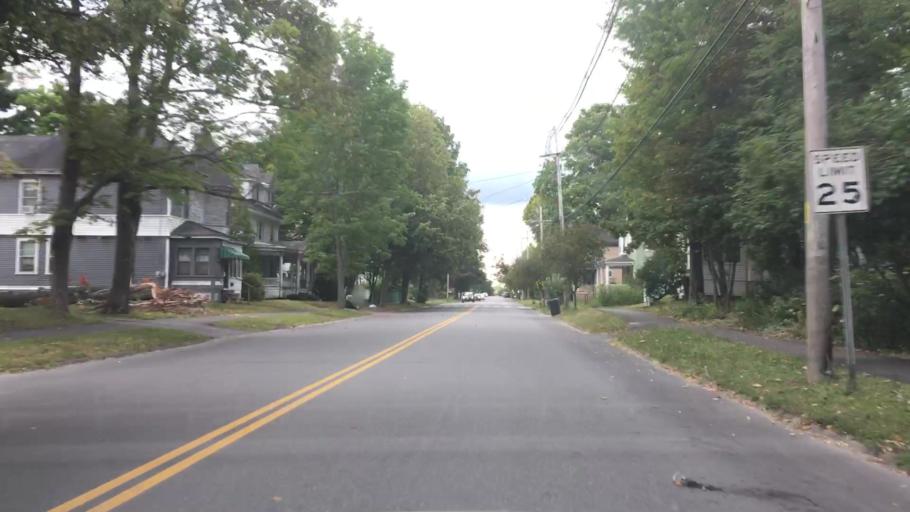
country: US
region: Maine
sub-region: Penobscot County
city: Bangor
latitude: 44.8171
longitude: -68.7741
